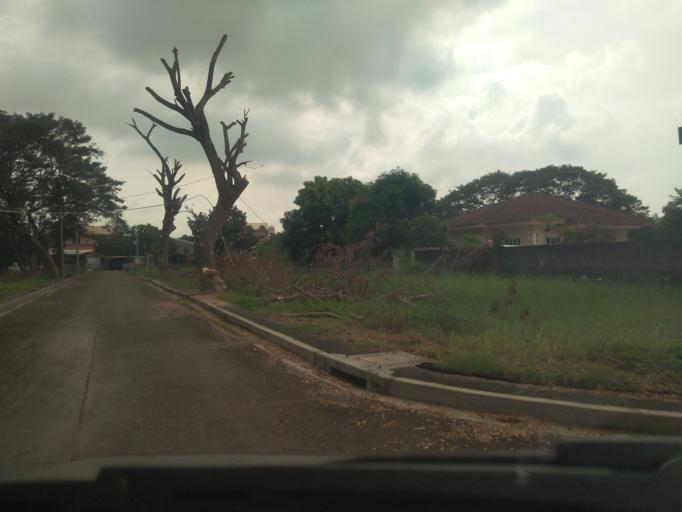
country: PH
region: Central Luzon
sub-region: Province of Pampanga
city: Santo Domingo
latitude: 15.0032
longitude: 120.7251
